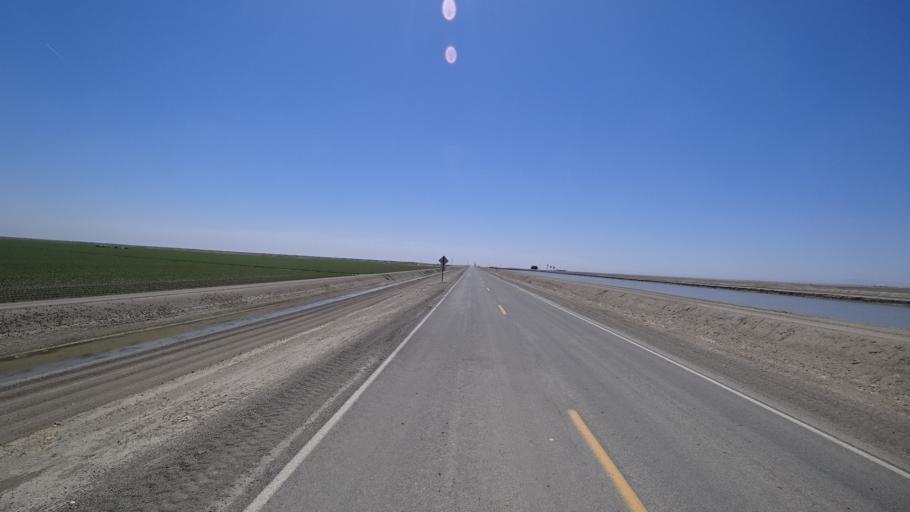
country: US
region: California
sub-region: Kings County
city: Corcoran
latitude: 36.0496
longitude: -119.6434
